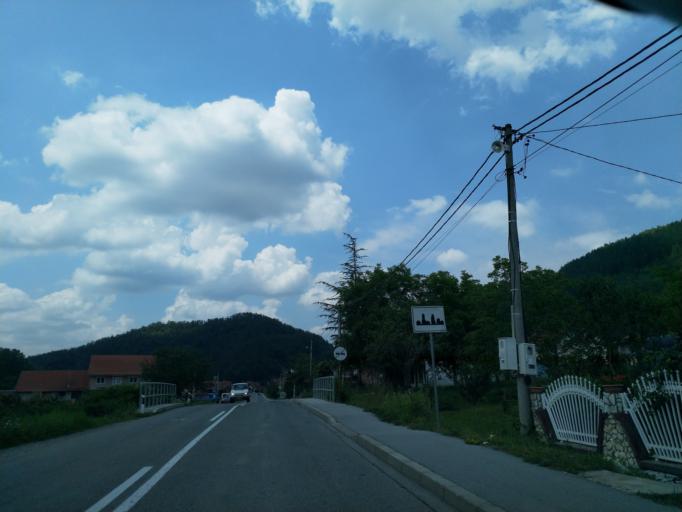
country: RS
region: Central Serbia
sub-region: Rasinski Okrug
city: Aleksandrovac
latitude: 43.3715
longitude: 21.0536
